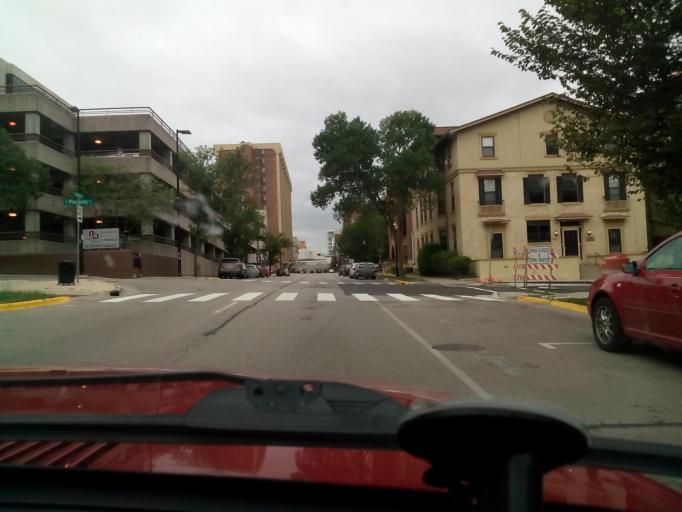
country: US
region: Wisconsin
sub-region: Dane County
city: Madison
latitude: 43.0773
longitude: -89.3847
